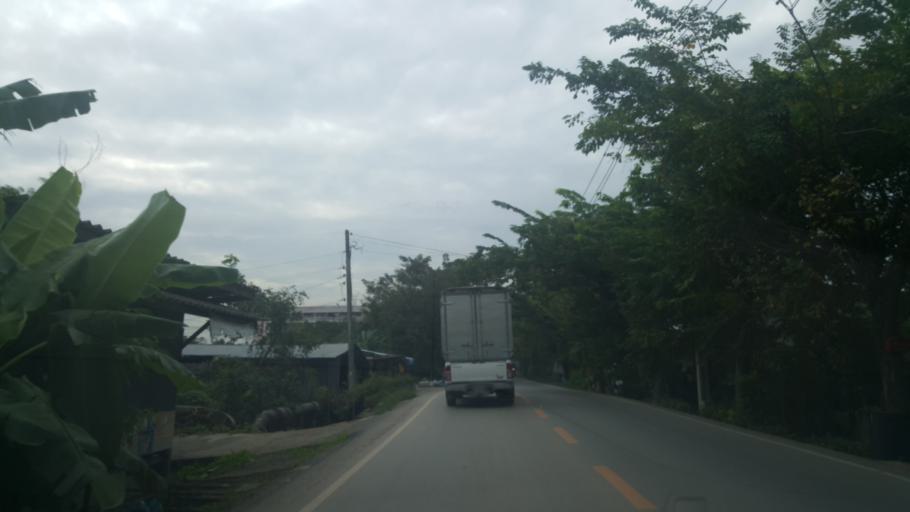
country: TH
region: Bangkok
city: Bang Khae
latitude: 13.6792
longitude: 100.3950
